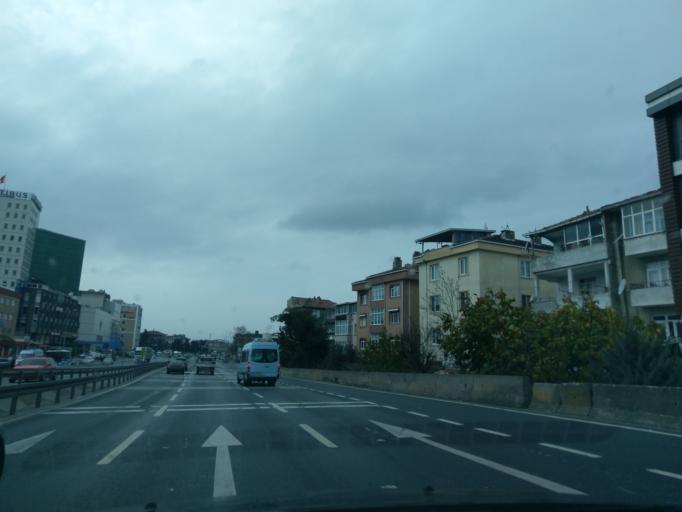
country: TR
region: Istanbul
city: Bueyuekcekmece
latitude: 41.0235
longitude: 28.5856
